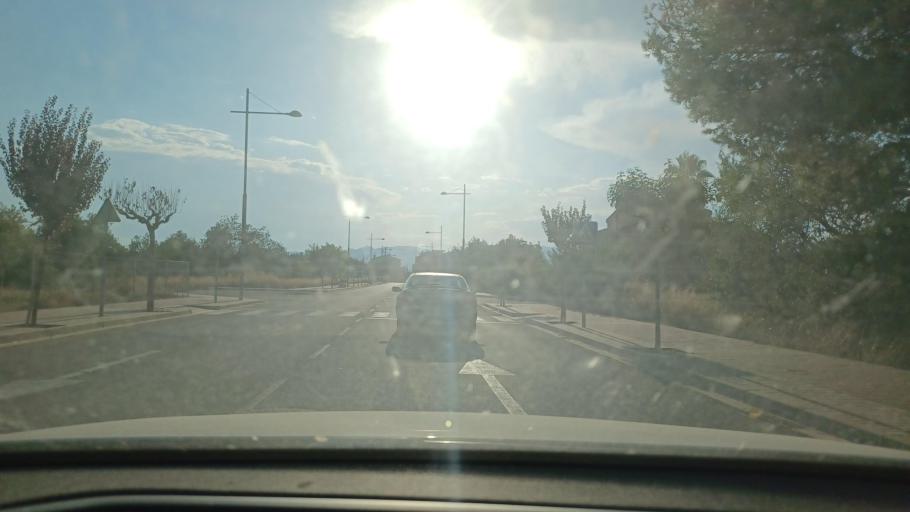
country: ES
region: Catalonia
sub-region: Provincia de Tarragona
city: Santa Barbara
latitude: 40.7125
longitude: 0.4993
